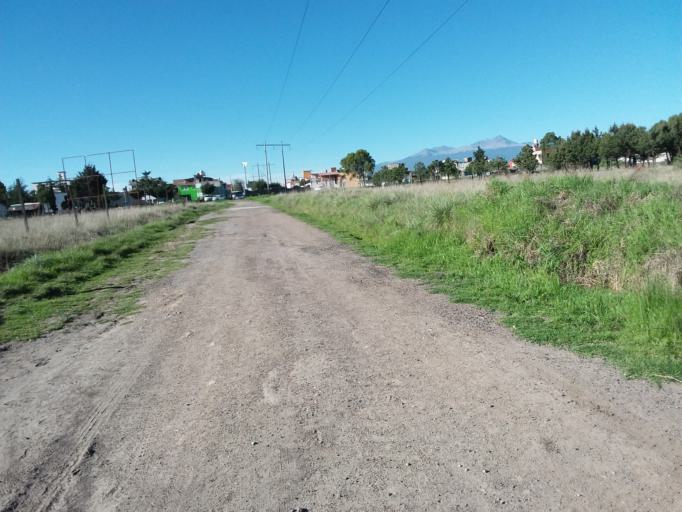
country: MX
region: Mexico
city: San Marcos Yachihuacaltepec
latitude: 19.3072
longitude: -99.6953
